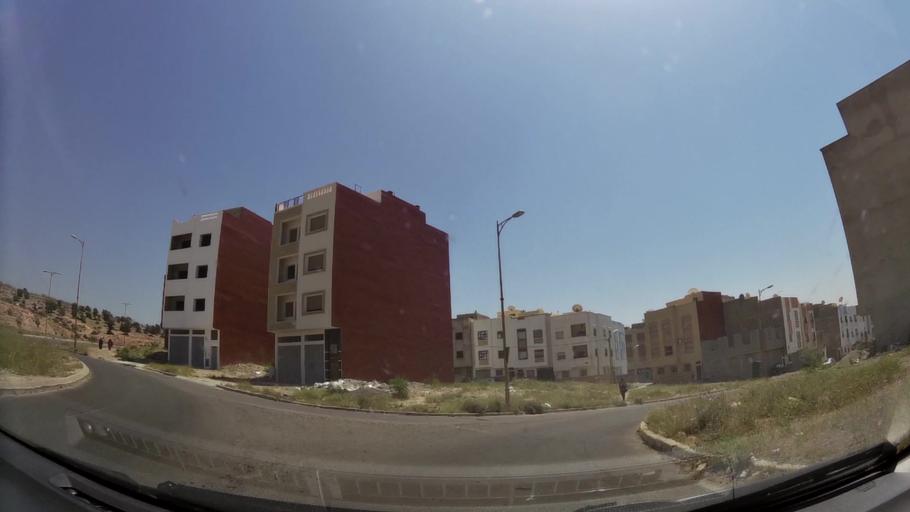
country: MA
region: Oued ed Dahab-Lagouira
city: Dakhla
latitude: 30.4362
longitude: -9.5483
